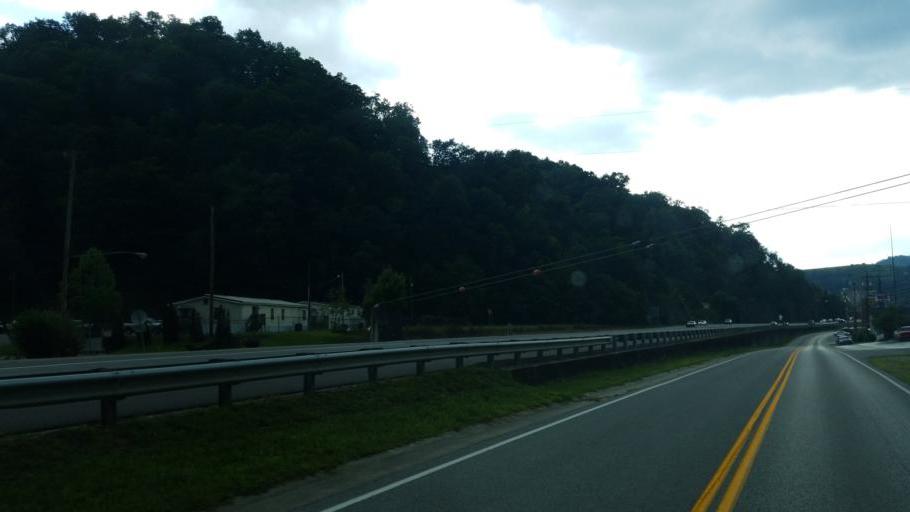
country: US
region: Kentucky
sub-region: Pike County
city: Pikeville
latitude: 37.4927
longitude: -82.5346
